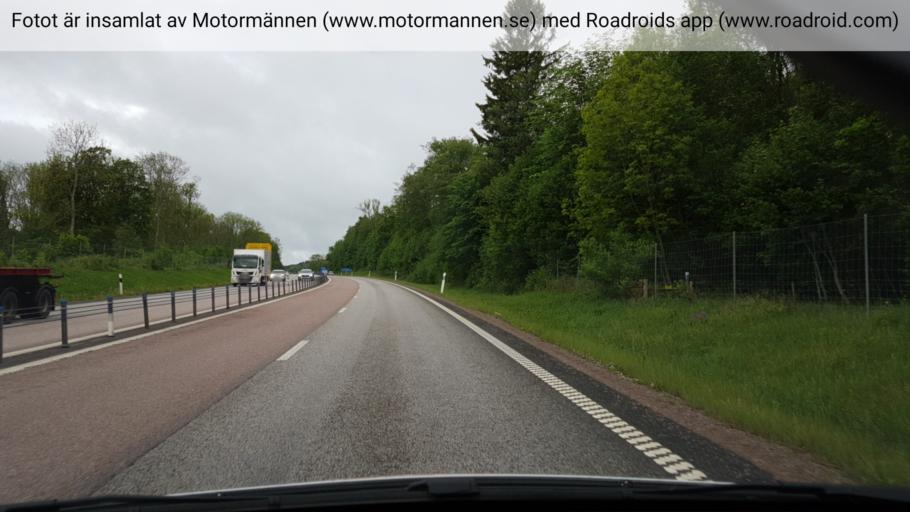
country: SE
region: Vaestra Goetaland
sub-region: Skovde Kommun
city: Skultorp
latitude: 58.3187
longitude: 13.8184
